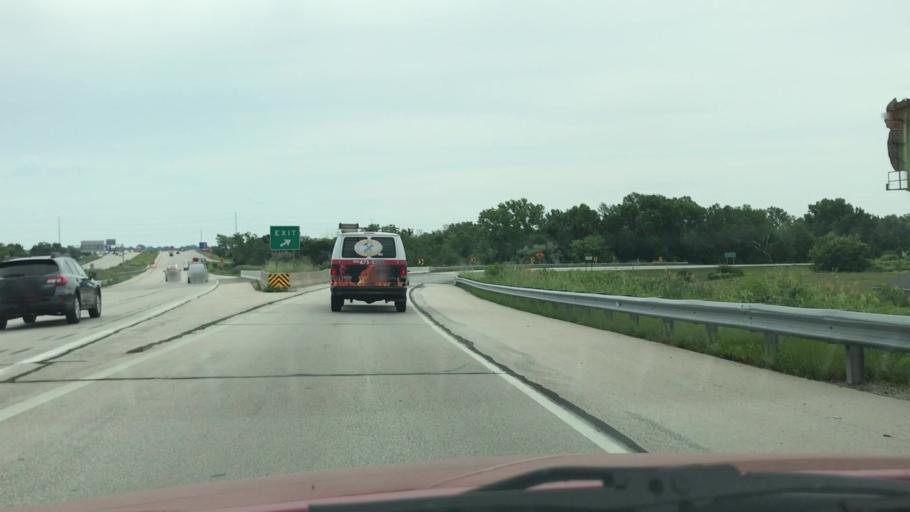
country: US
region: Wisconsin
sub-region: Brown County
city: Ashwaubenon
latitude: 44.4795
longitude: -88.0681
